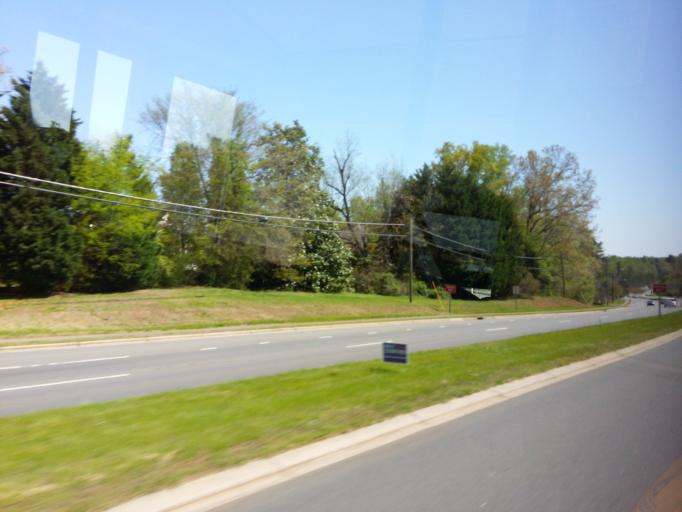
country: US
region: North Carolina
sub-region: Orange County
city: Chapel Hill
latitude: 35.9574
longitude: -79.0578
